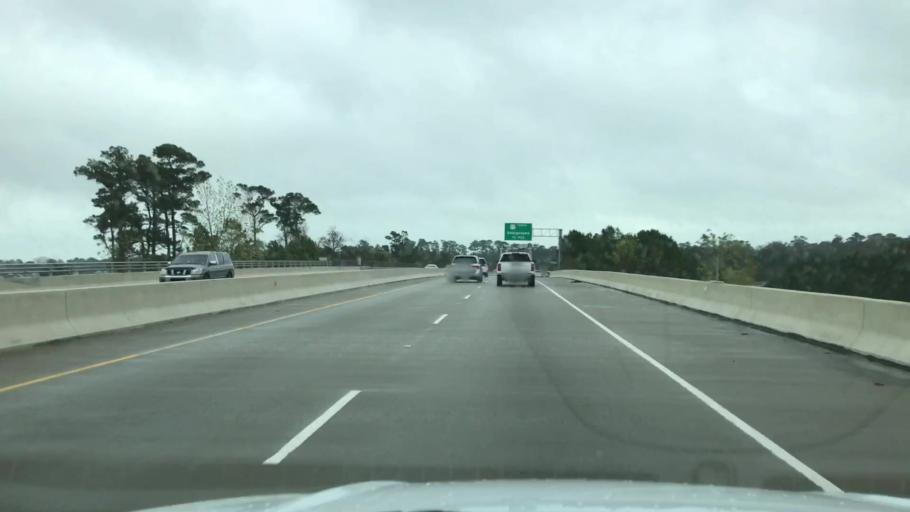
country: US
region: South Carolina
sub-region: Horry County
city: Myrtle Beach
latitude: 33.7497
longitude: -78.8492
